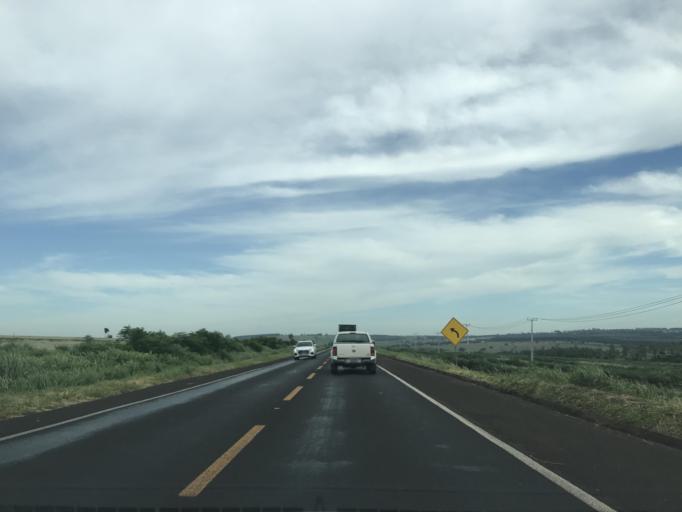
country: BR
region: Parana
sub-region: Paranavai
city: Paranavai
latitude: -23.0076
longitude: -52.5437
